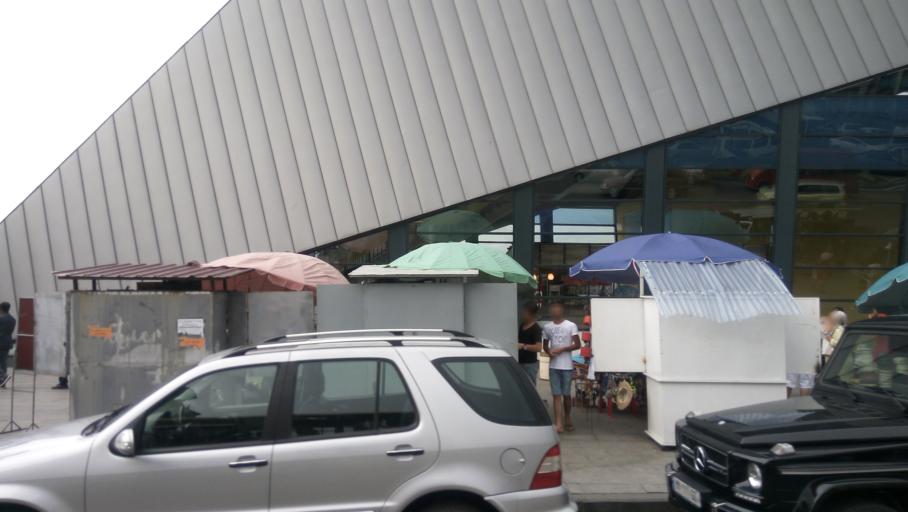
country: GE
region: Ajaria
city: Batumi
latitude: 41.6475
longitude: 41.6453
